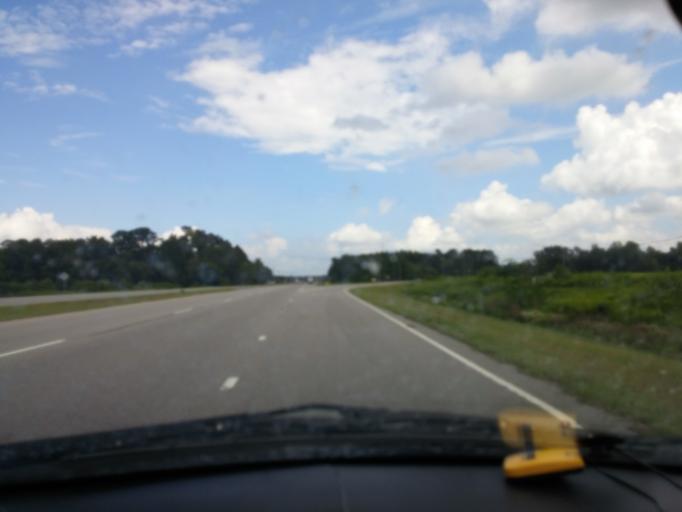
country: US
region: North Carolina
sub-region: Pitt County
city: Grifton
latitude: 35.3622
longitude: -77.4624
